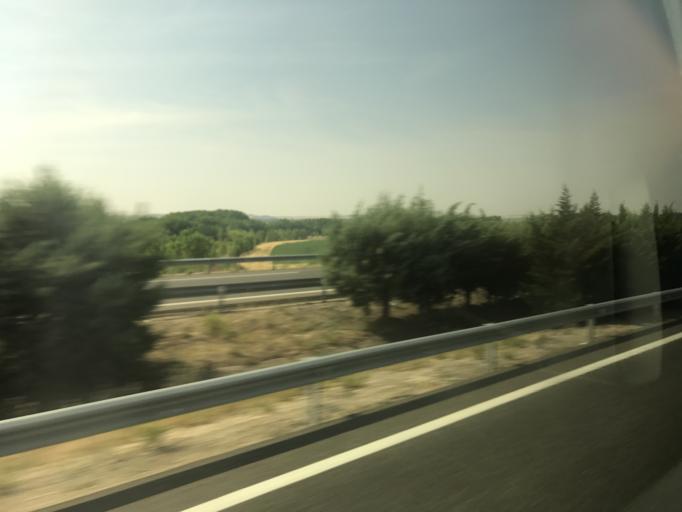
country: ES
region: Castille and Leon
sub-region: Provincia de Palencia
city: Quintana del Puente
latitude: 42.1090
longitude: -4.1751
